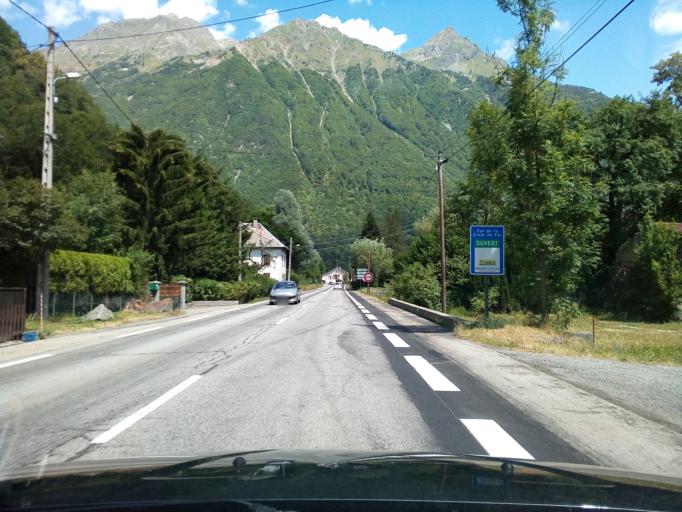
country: FR
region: Rhone-Alpes
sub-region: Departement de l'Isere
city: Huez
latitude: 45.1116
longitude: 6.0065
